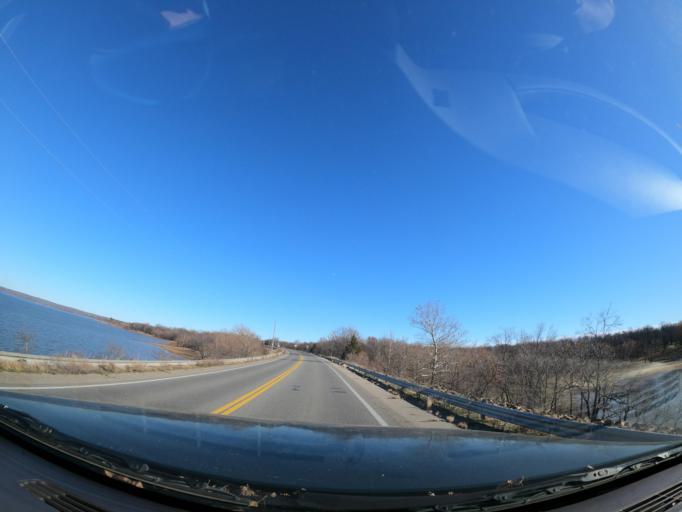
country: US
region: Oklahoma
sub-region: Pittsburg County
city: Longtown
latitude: 35.2395
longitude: -95.5548
